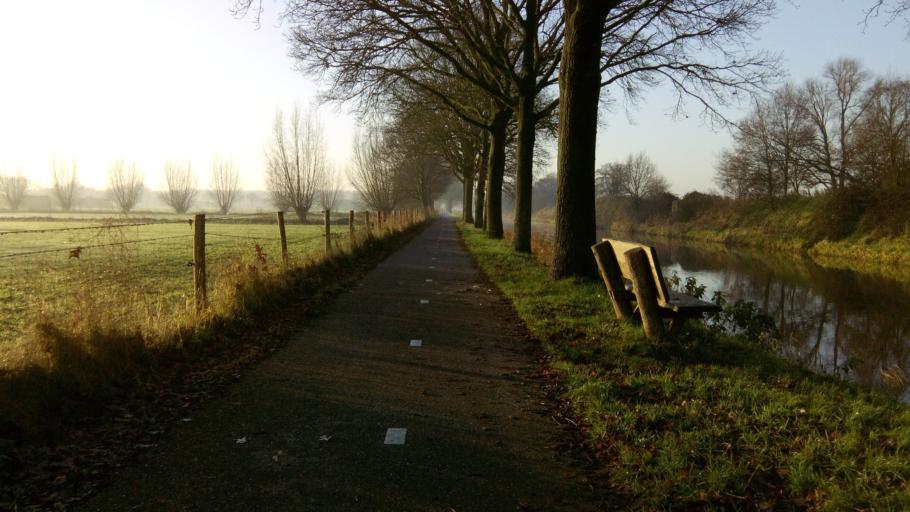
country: NL
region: Utrecht
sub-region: Gemeente Leusden
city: Leusden
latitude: 52.1198
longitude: 5.4441
